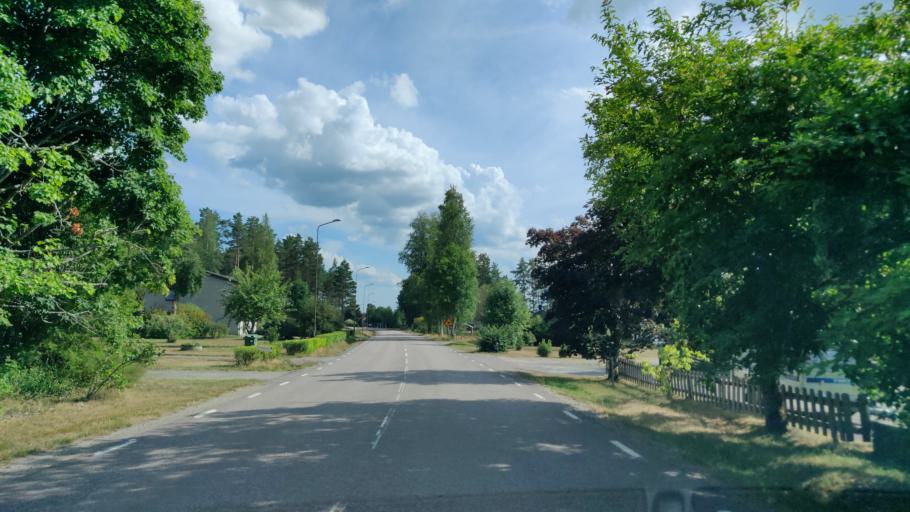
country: SE
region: Vaermland
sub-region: Hagfors Kommun
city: Ekshaerad
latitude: 60.1164
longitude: 13.5629
